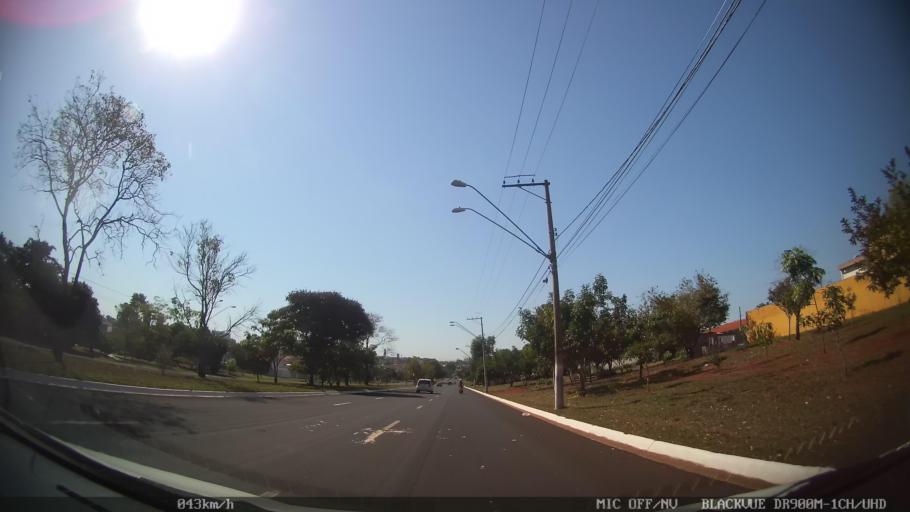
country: BR
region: Sao Paulo
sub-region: Ribeirao Preto
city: Ribeirao Preto
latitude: -21.2136
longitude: -47.7786
